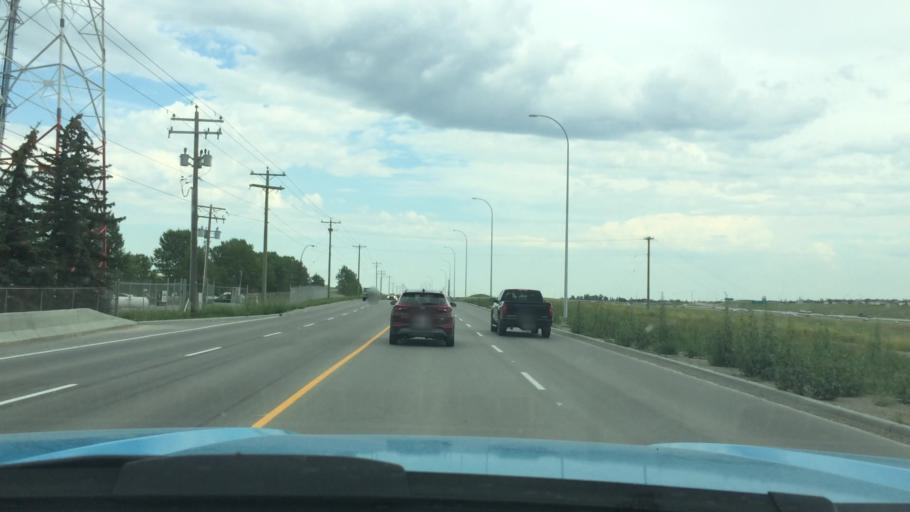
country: CA
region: Alberta
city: Calgary
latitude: 51.1542
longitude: -114.1864
